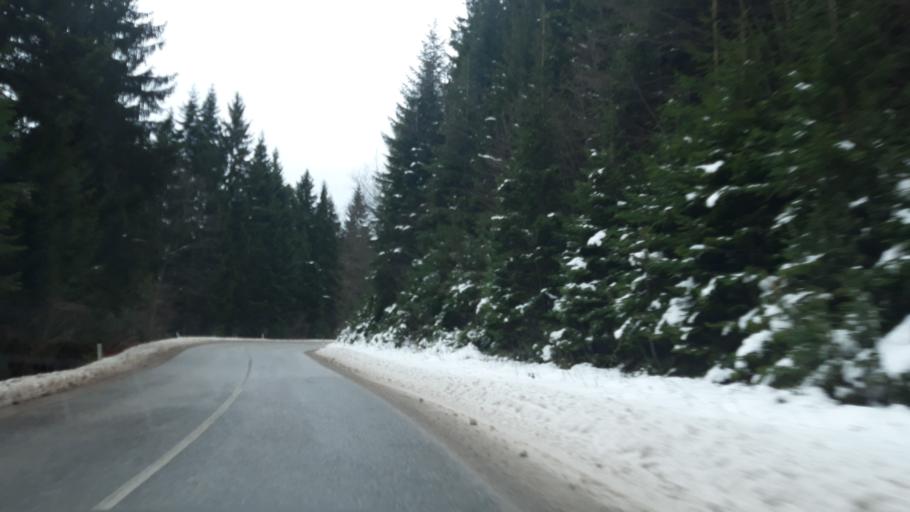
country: BA
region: Republika Srpska
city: Koran
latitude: 43.8007
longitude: 18.5505
